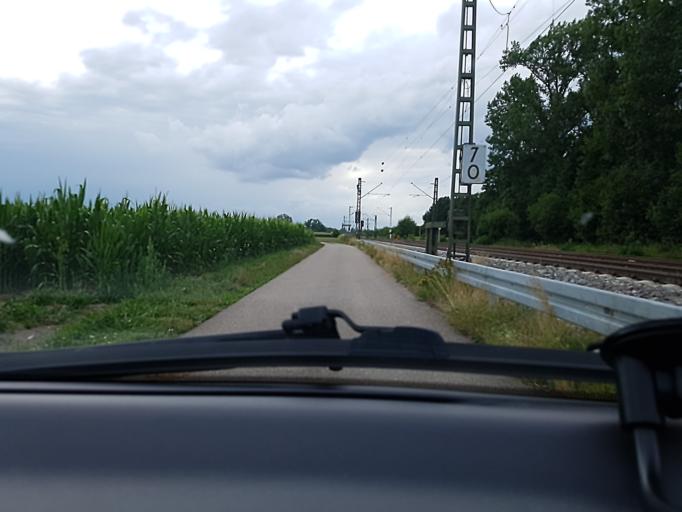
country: DE
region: Baden-Wuerttemberg
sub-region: Freiburg Region
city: Willstatt
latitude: 48.5655
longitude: 7.8901
